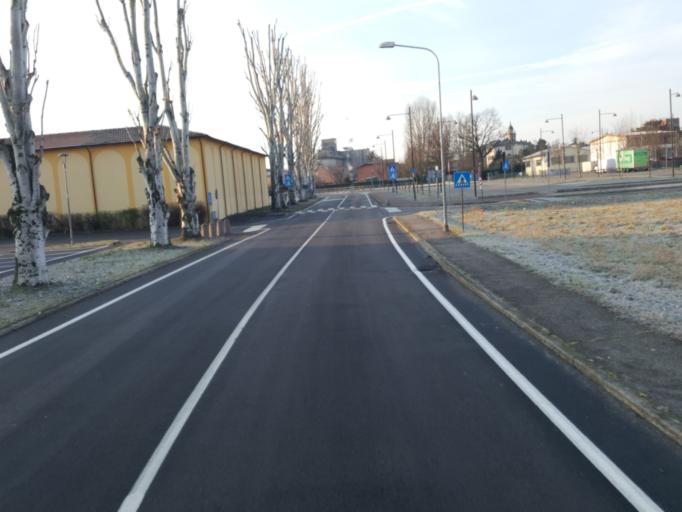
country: IT
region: Emilia-Romagna
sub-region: Provincia di Parma
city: Sorbolo
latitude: 44.8494
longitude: 10.4524
